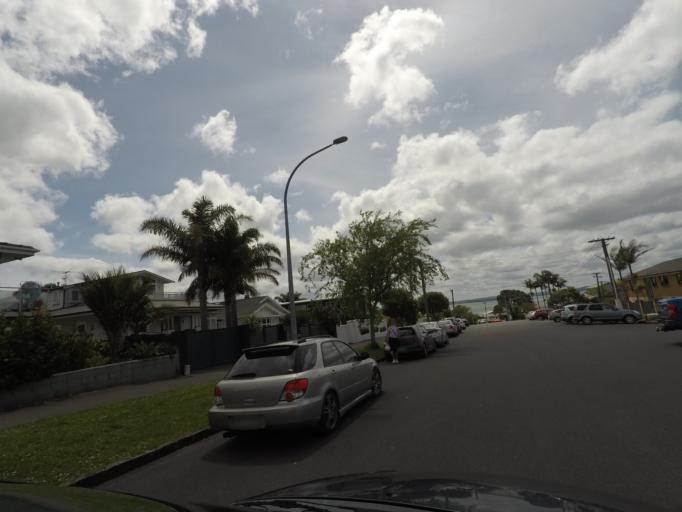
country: NZ
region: Auckland
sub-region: Auckland
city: Auckland
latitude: -36.8536
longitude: 174.7177
